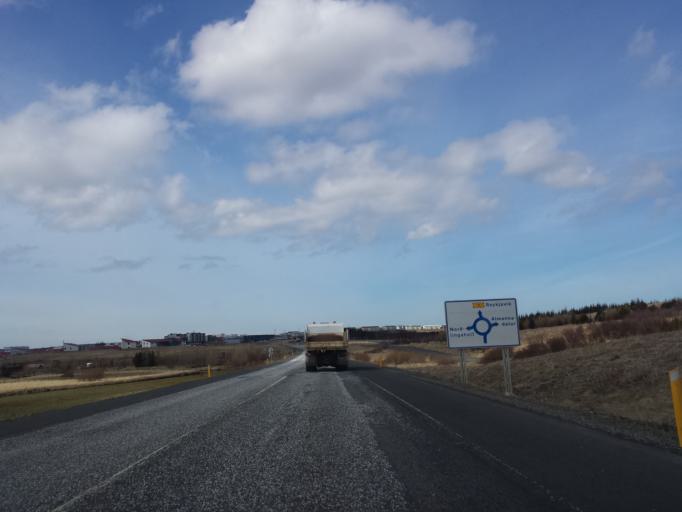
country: IS
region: Capital Region
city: Mosfellsbaer
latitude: 64.0999
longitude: -21.7517
